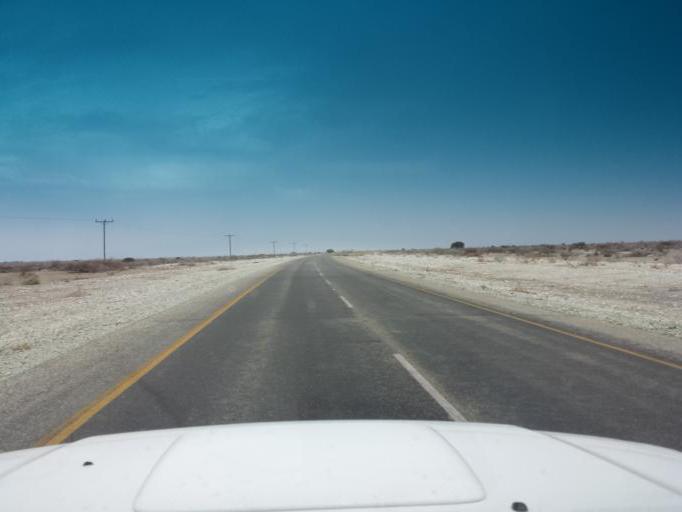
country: BW
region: Central
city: Mopipi
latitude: -21.1346
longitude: 24.6888
